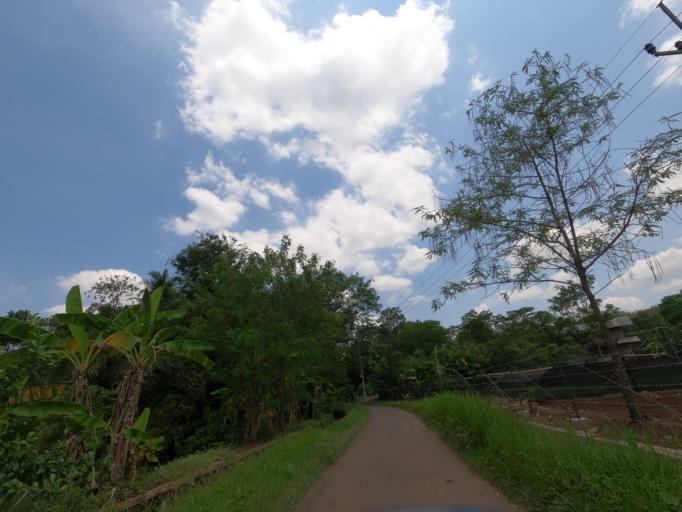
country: ID
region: West Java
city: Pamanukan
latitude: -6.5059
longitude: 107.7715
